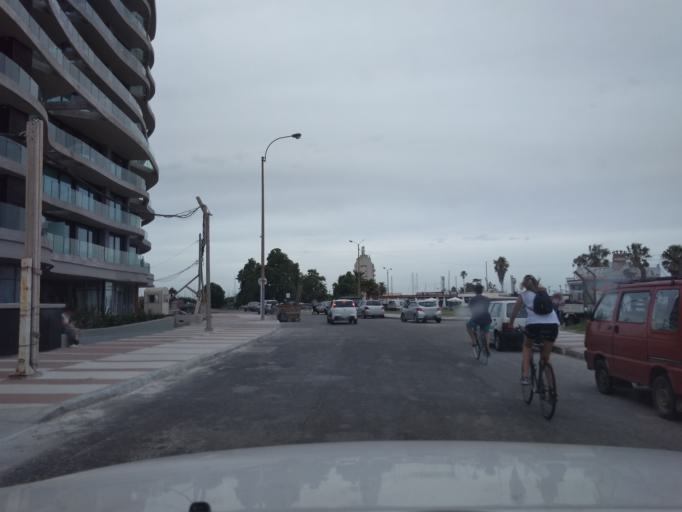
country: UY
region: Montevideo
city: Montevideo
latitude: -34.9106
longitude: -56.1340
